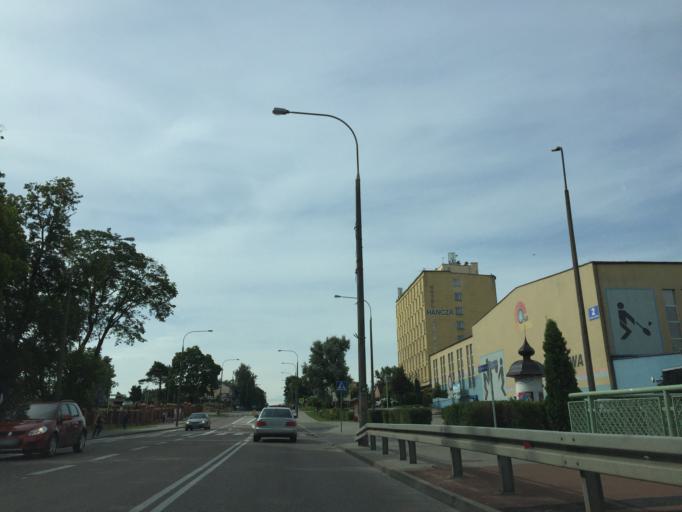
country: PL
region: Podlasie
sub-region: Suwalki
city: Suwalki
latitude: 54.0936
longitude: 22.9289
